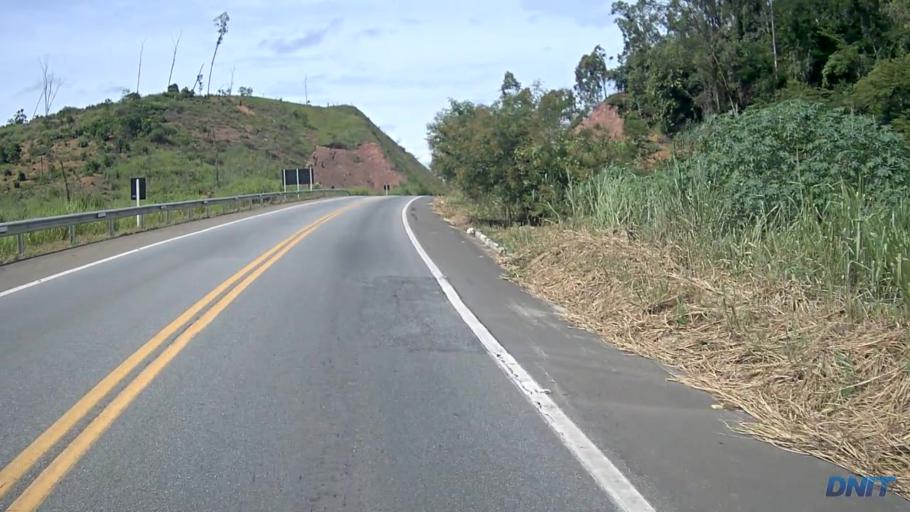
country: BR
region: Minas Gerais
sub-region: Ipatinga
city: Ipatinga
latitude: -19.4360
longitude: -42.5097
